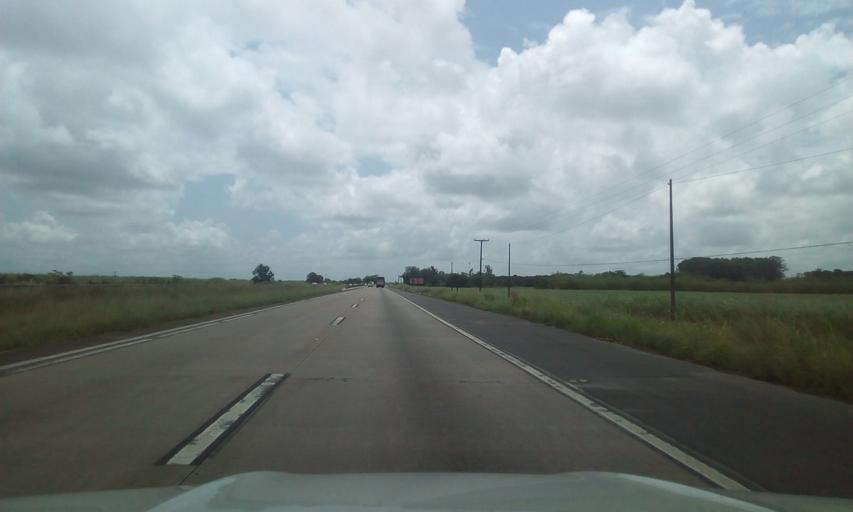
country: BR
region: Pernambuco
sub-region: Goiana
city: Goiana
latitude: -7.6525
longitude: -34.9456
